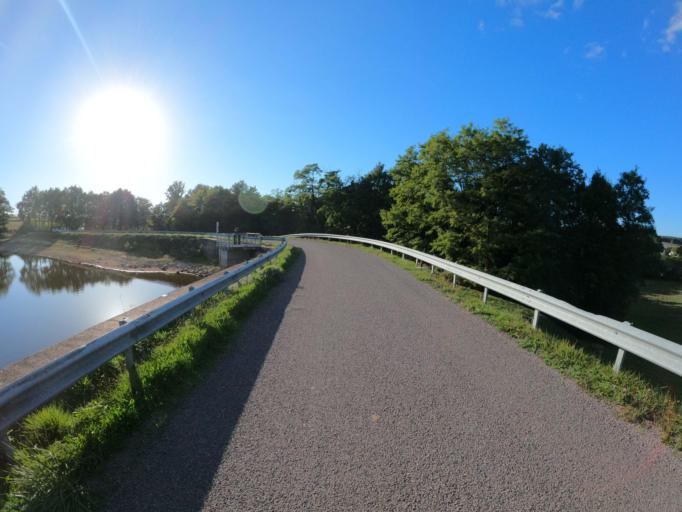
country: FR
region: Bourgogne
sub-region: Departement de Saone-et-Loire
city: Ecuisses
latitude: 46.7529
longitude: 4.5140
